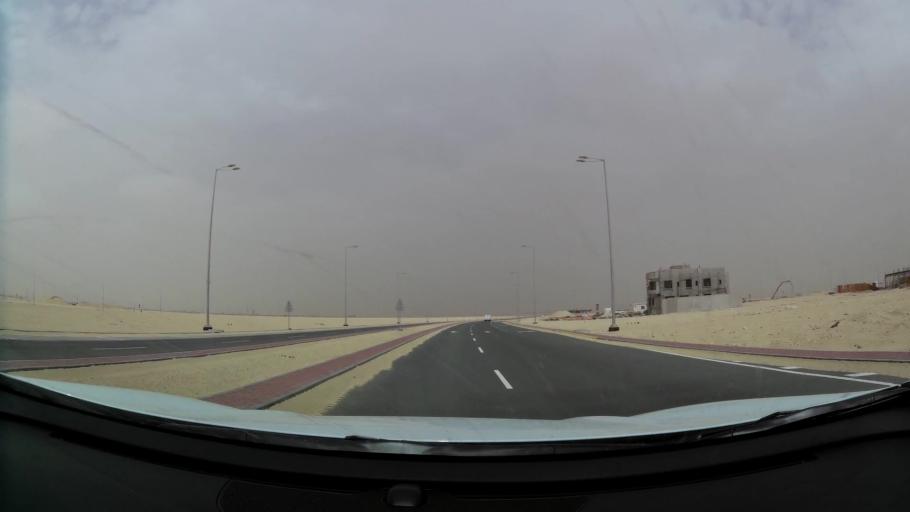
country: AE
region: Abu Dhabi
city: Abu Dhabi
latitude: 24.3565
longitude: 54.7422
